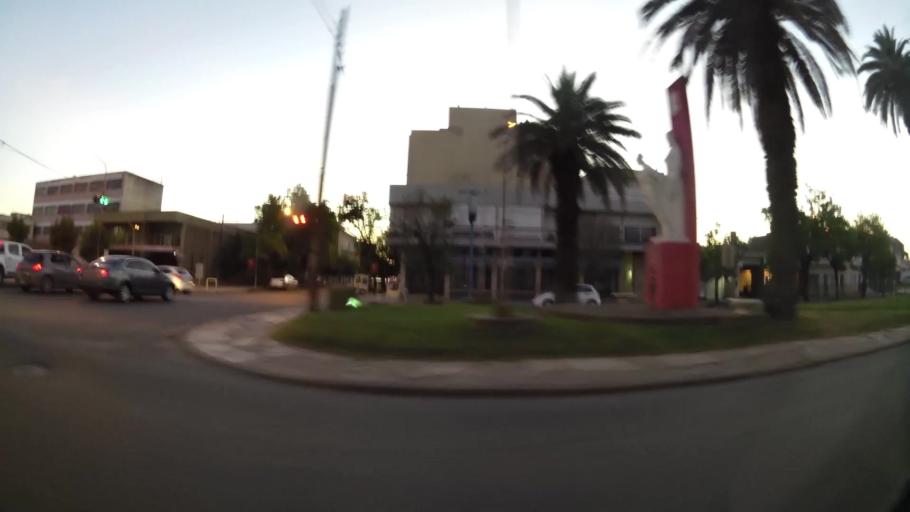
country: AR
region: Cordoba
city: Villa Maria
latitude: -32.4082
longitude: -63.2390
